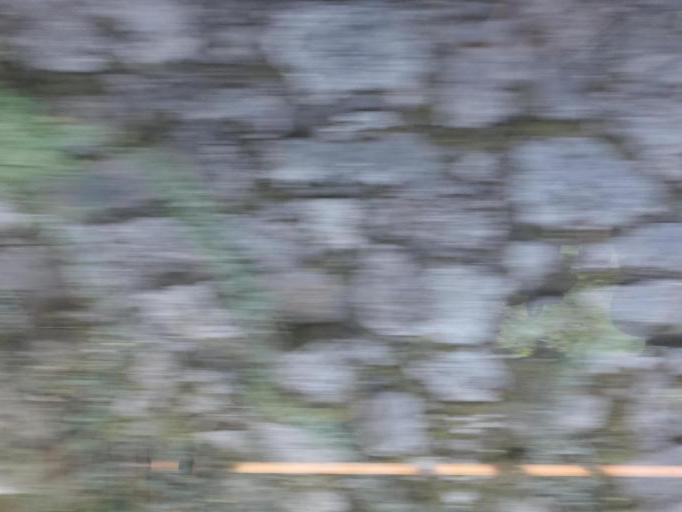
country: CH
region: Valais
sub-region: Martigny District
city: Martigny-Combe
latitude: 46.0756
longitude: 7.0695
